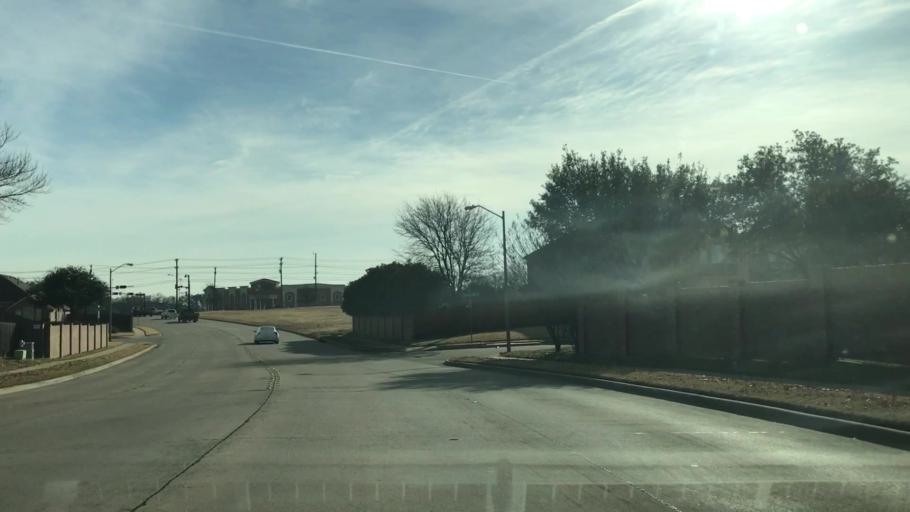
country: US
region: Texas
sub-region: Tarrant County
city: Colleyville
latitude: 32.8917
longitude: -97.2057
